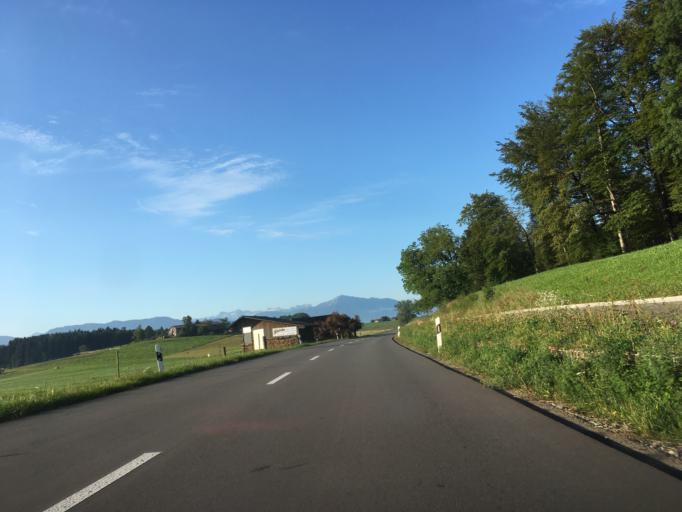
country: CH
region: Zurich
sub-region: Bezirk Affoltern
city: Hausen am Albis / Hausen (Dorf)
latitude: 47.2403
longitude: 8.5316
